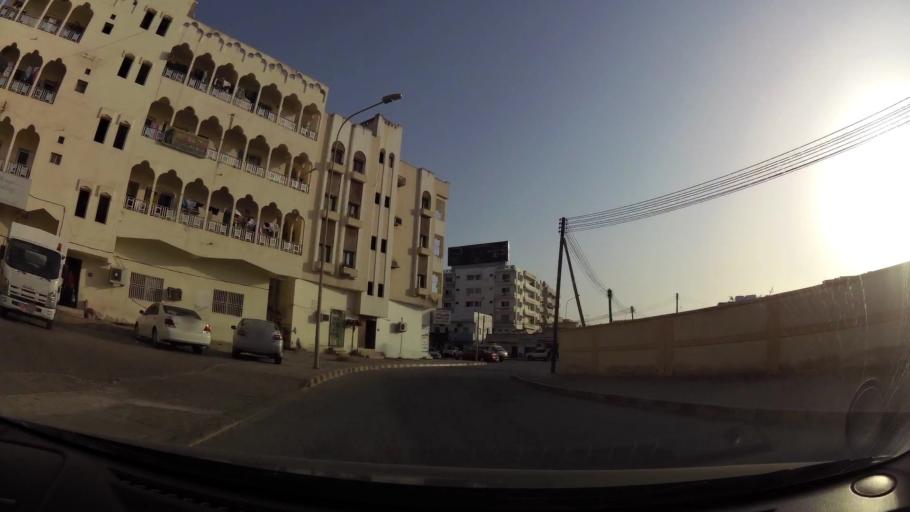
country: OM
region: Zufar
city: Salalah
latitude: 17.0141
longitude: 54.0965
